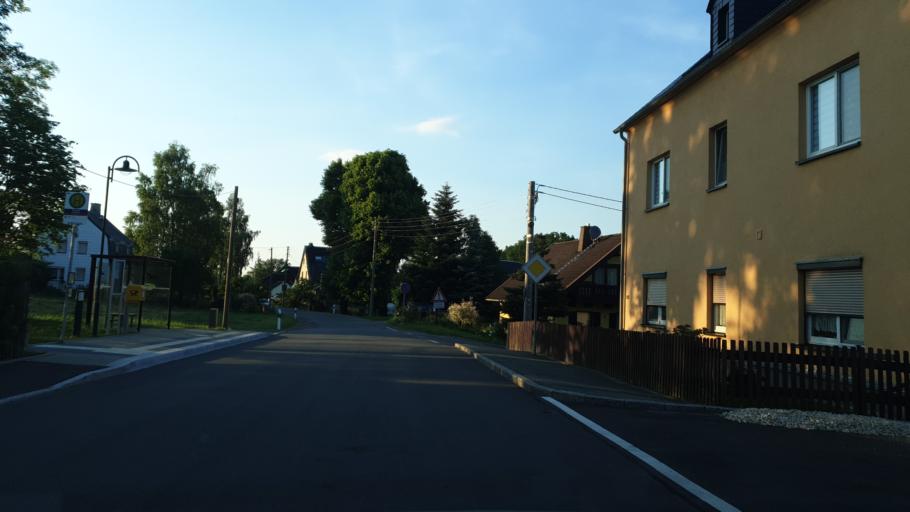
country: DE
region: Saxony
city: Stollberg
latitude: 50.6779
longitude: 12.7406
